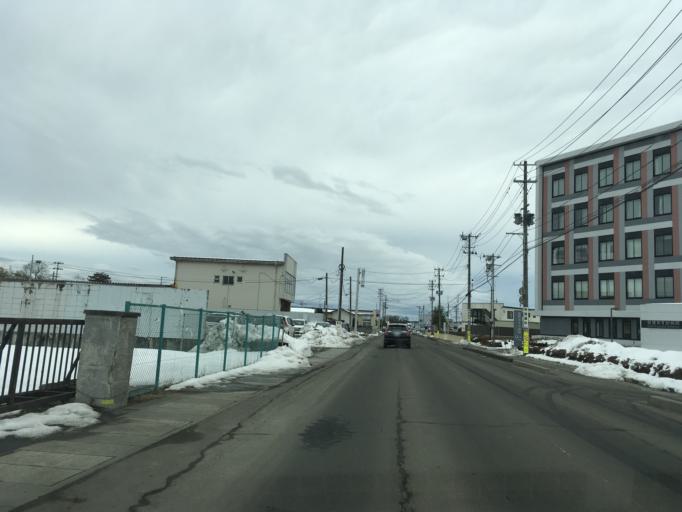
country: JP
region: Miyagi
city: Furukawa
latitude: 38.5566
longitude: 140.9535
